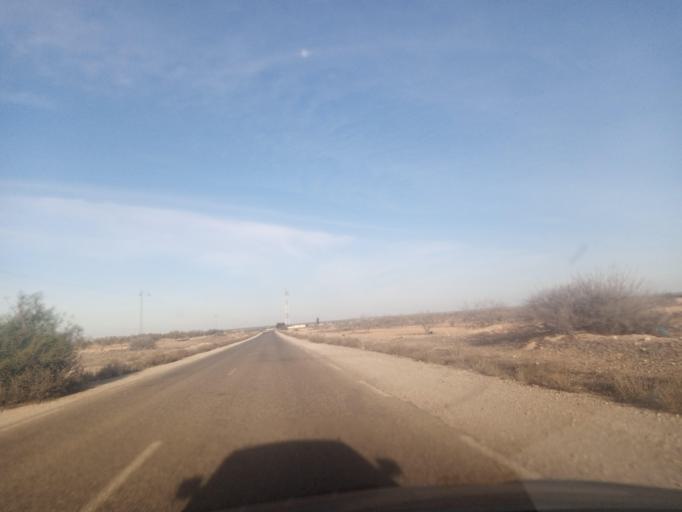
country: TN
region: Safaqis
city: Bi'r `Ali Bin Khalifah
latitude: 34.9405
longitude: 10.3433
